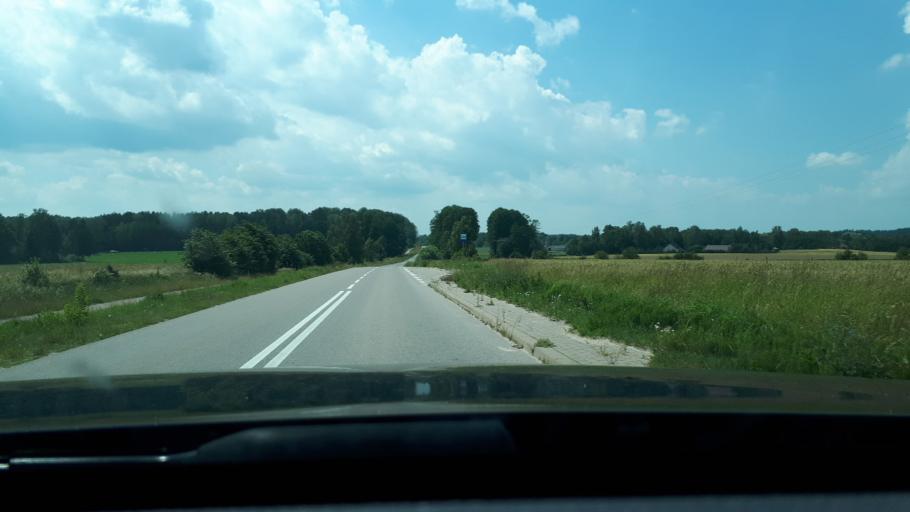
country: PL
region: Podlasie
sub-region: Powiat bialostocki
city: Choroszcz
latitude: 53.1251
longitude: 22.9633
